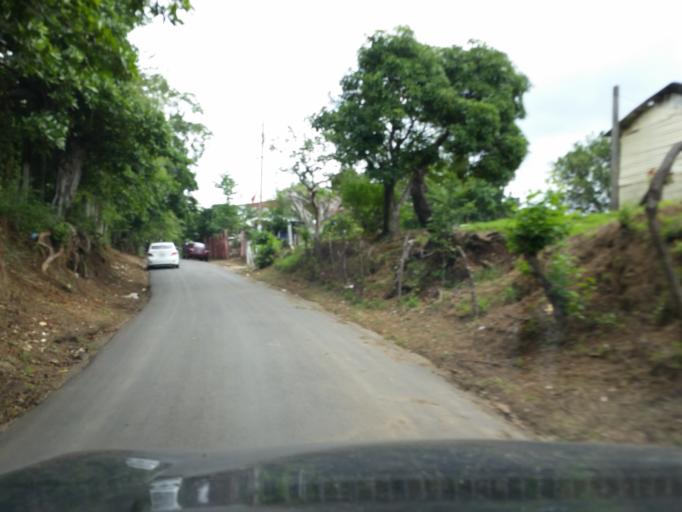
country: NI
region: Managua
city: Managua
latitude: 12.1019
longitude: -86.2787
